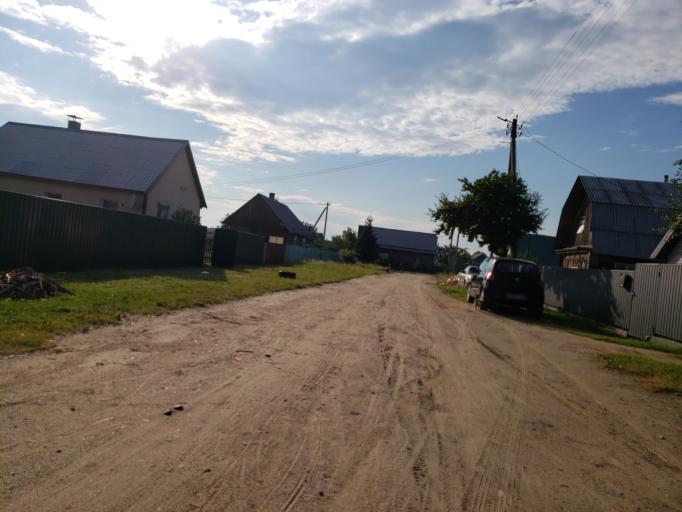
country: BY
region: Minsk
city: Chervyen'
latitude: 53.7029
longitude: 28.4430
